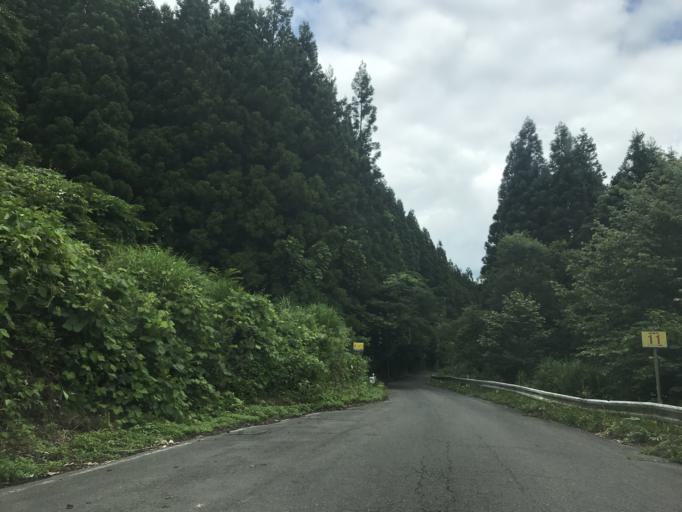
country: JP
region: Iwate
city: Ichinoseki
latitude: 38.9646
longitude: 140.9040
